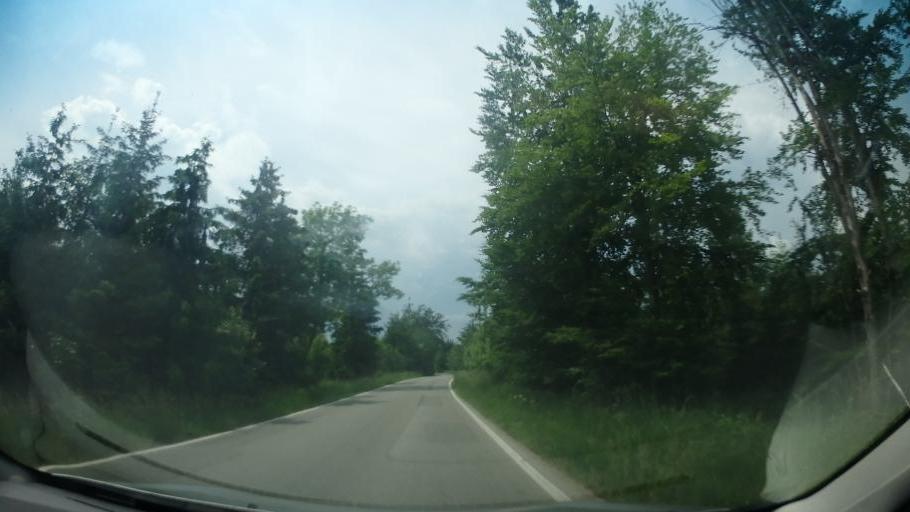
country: CZ
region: South Moravian
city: Lysice
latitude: 49.4581
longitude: 16.4865
